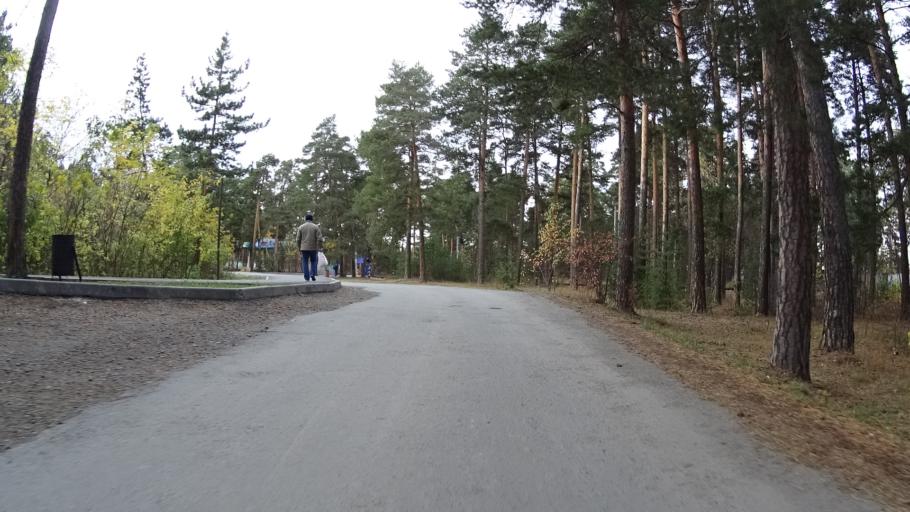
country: RU
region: Chelyabinsk
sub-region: Gorod Chelyabinsk
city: Chelyabinsk
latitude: 55.1676
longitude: 61.3644
